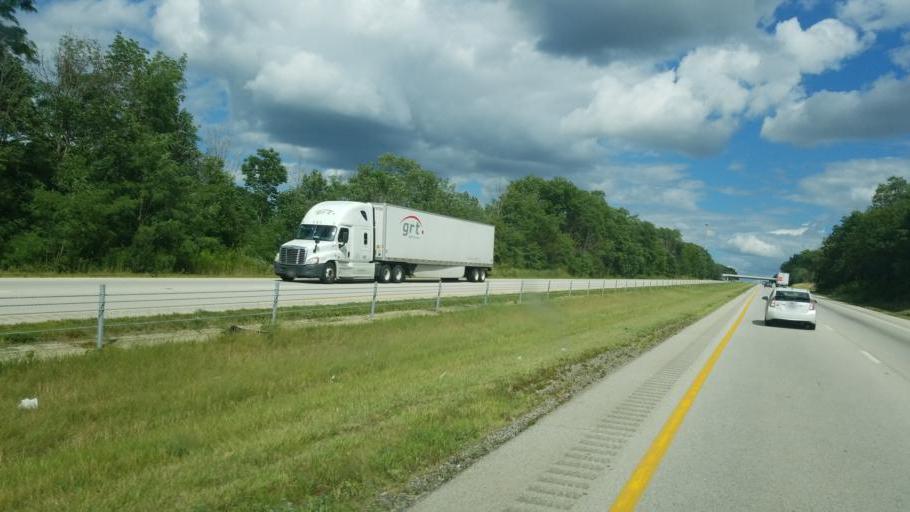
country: US
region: Ohio
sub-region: Medina County
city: Seville
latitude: 41.0325
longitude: -81.8395
